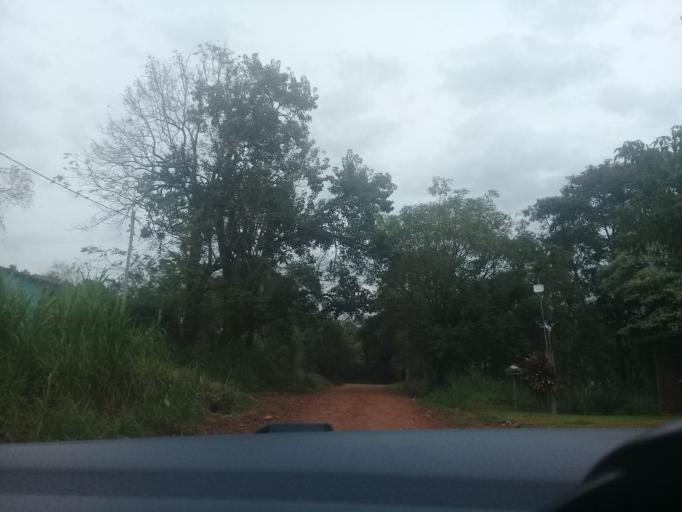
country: AR
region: Misiones
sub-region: Departamento de Obera
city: Obera
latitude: -27.4790
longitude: -55.1526
